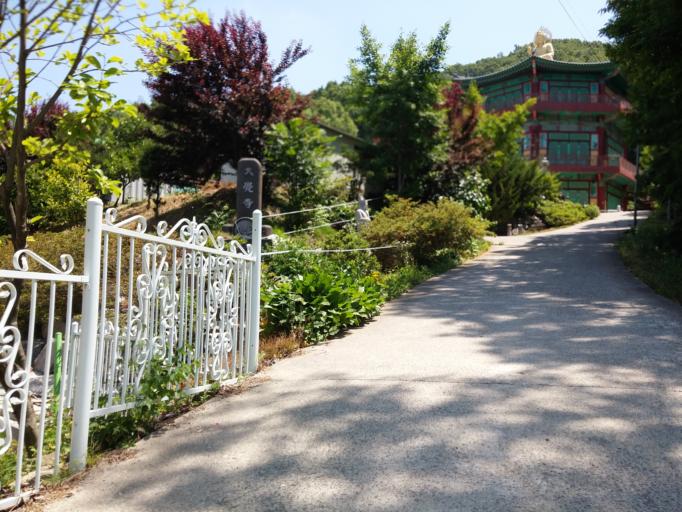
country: KR
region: Chungcheongbuk-do
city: Cheongju-si
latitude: 36.5553
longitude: 127.4390
